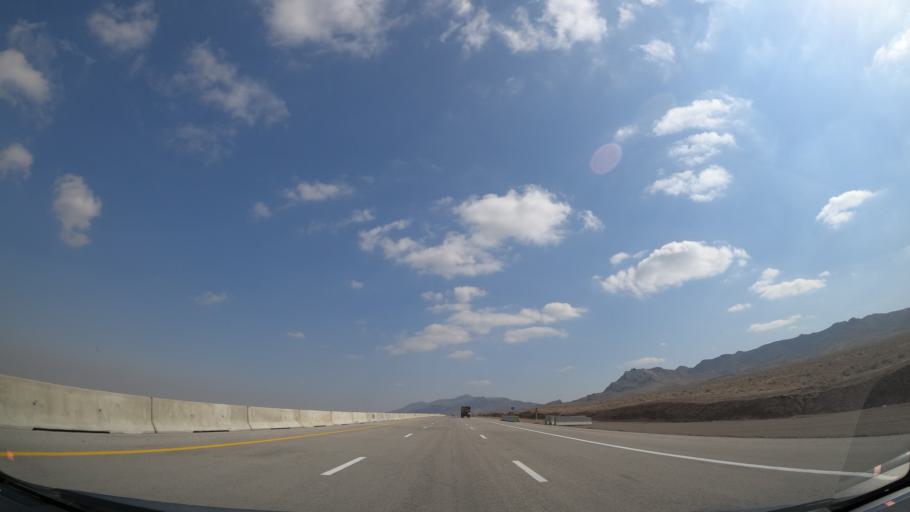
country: IR
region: Alborz
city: Eshtehard
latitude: 35.7098
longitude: 50.5984
